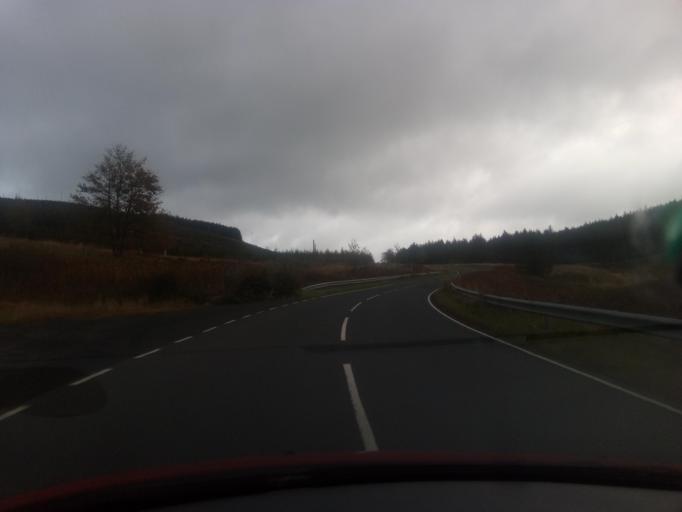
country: GB
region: Scotland
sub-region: The Scottish Borders
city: Hawick
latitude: 55.3146
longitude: -2.6539
